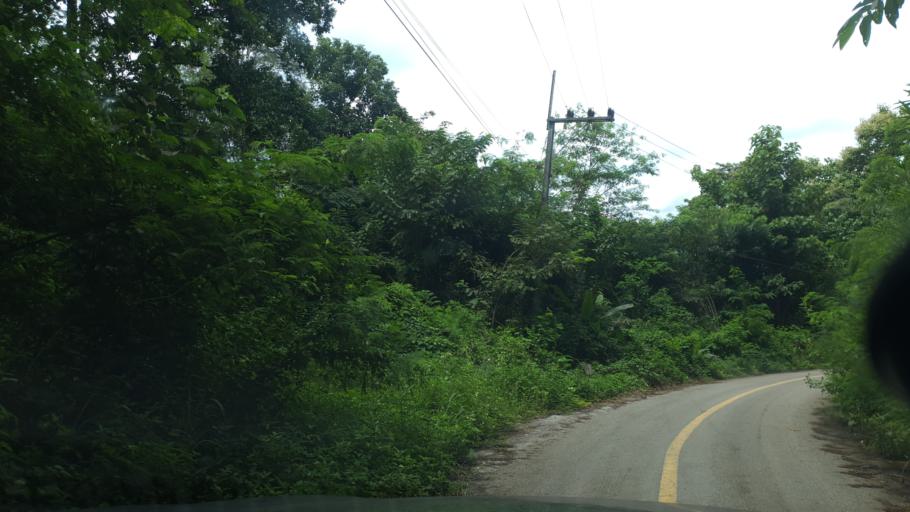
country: TH
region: Lampang
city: Hang Chat
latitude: 18.3533
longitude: 99.2530
